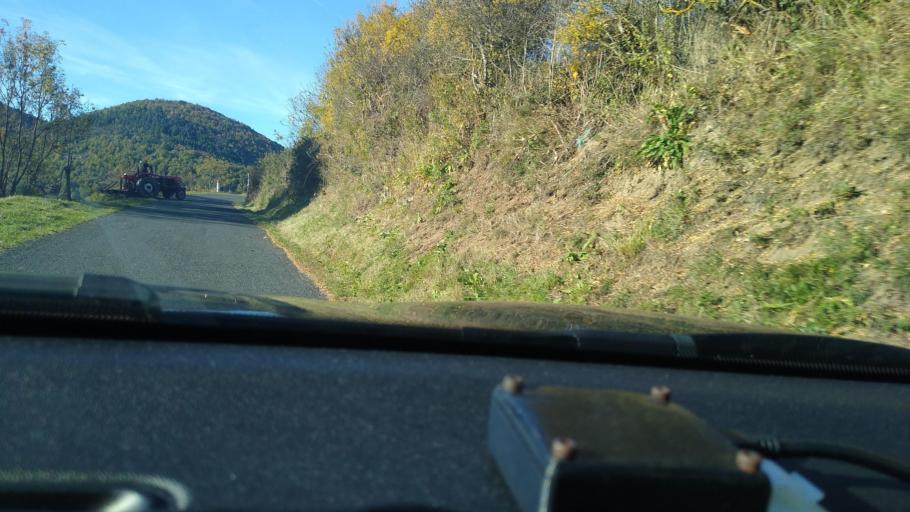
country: FR
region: Languedoc-Roussillon
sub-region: Departement de l'Aude
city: Quillan
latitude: 42.7340
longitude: 2.1260
